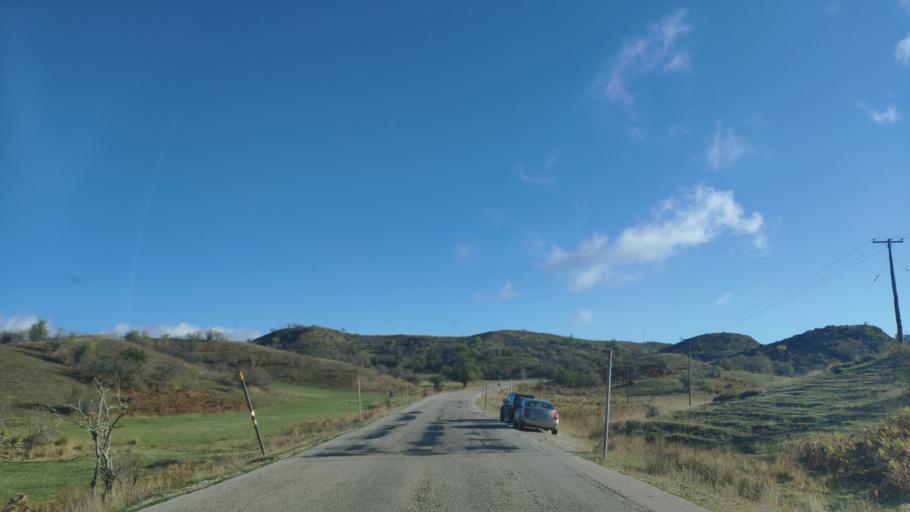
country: GR
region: Epirus
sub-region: Nomos Ioanninon
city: Metsovo
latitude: 39.7878
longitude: 21.1592
